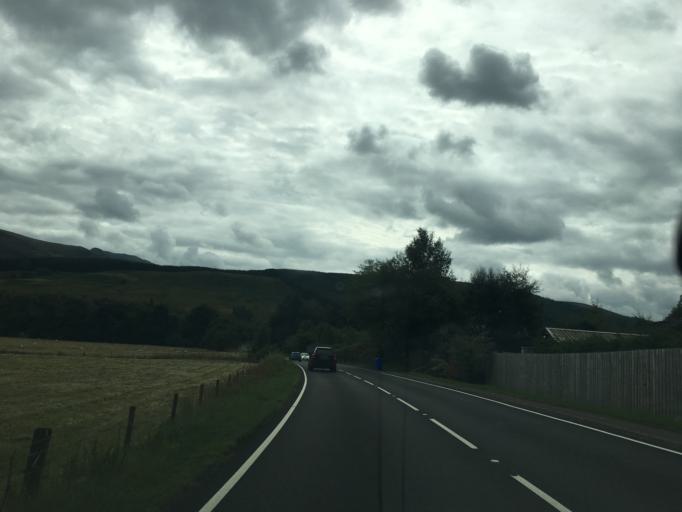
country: GB
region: Scotland
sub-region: Stirling
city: Callander
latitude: 56.3816
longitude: -4.2869
